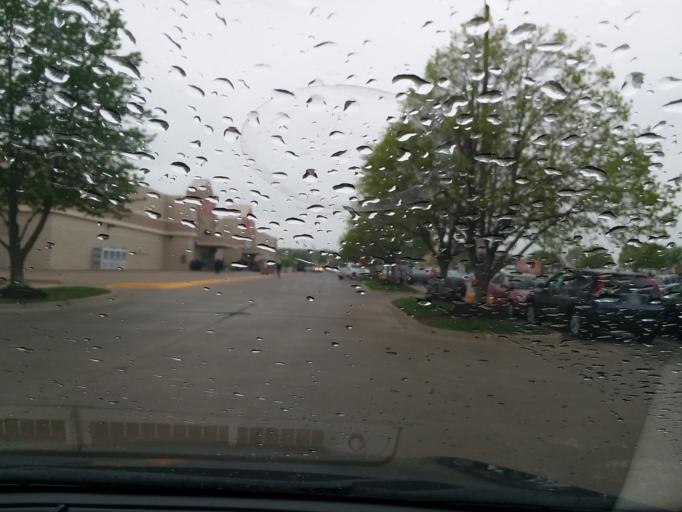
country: US
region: Kansas
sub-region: Douglas County
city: Lawrence
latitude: 38.9706
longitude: -95.3031
